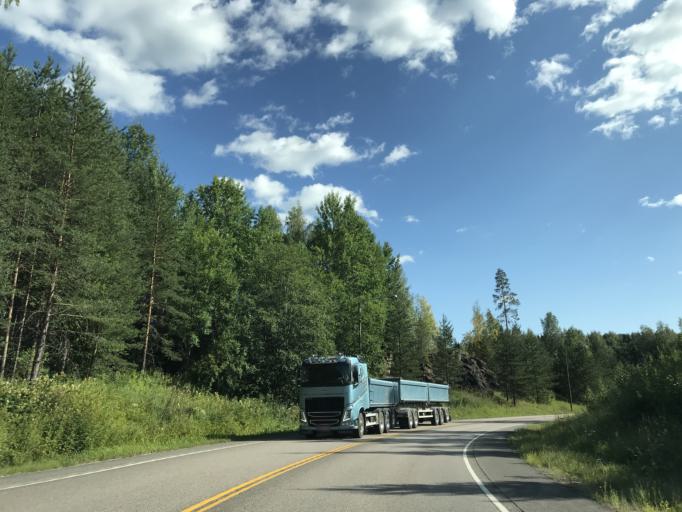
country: FI
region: Uusimaa
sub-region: Helsinki
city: Nurmijaervi
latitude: 60.4589
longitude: 24.8354
